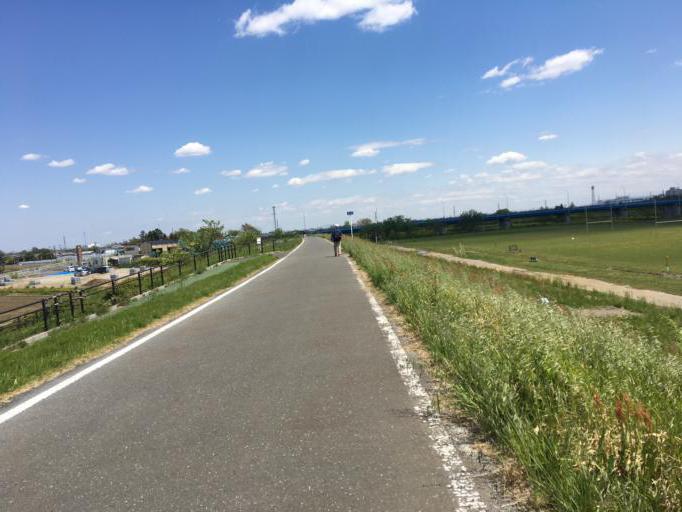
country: JP
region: Saitama
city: Kawagoe
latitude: 35.9324
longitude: 139.4578
